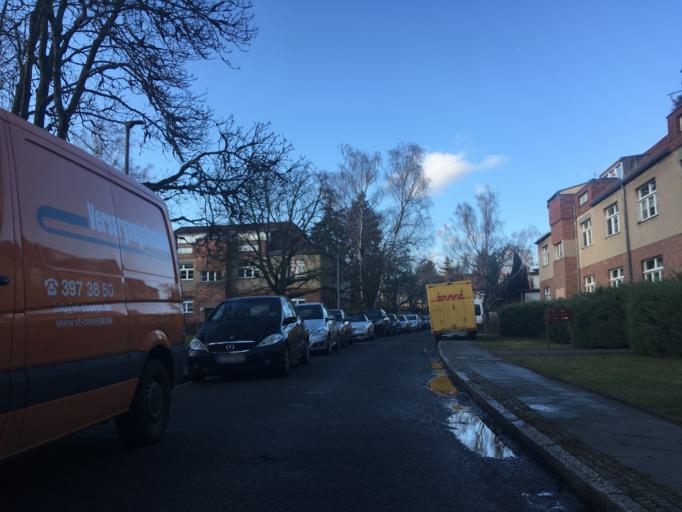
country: DE
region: Berlin
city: Wittenau
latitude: 52.5910
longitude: 13.3113
